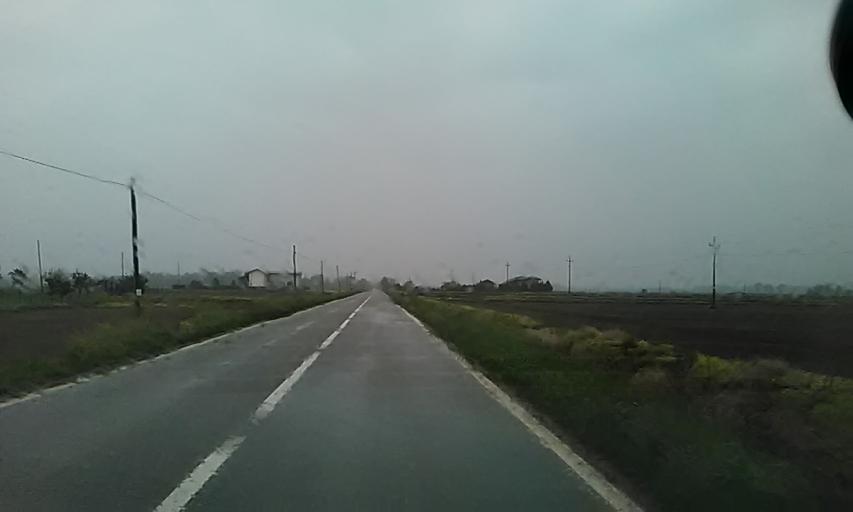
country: IT
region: Piedmont
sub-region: Provincia di Vercelli
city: Arborio
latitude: 45.4974
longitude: 8.3651
